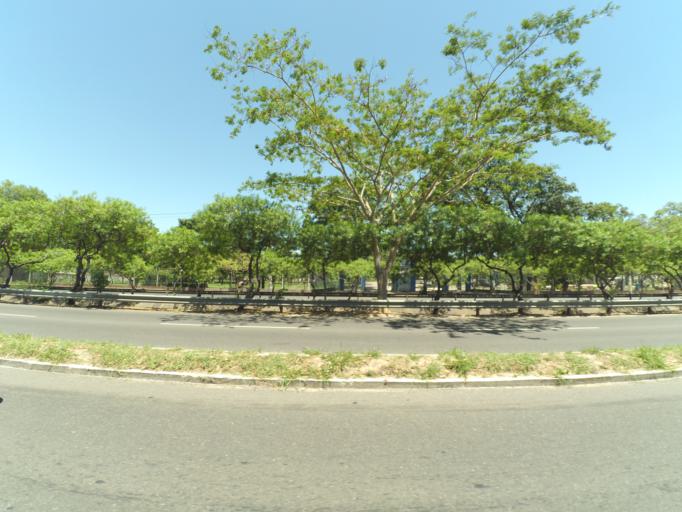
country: BO
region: Santa Cruz
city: Santa Cruz de la Sierra
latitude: -17.7780
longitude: -63.1931
